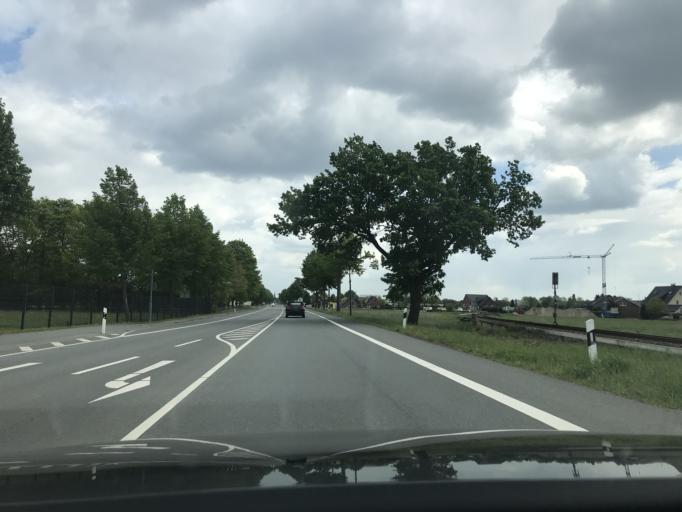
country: DE
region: North Rhine-Westphalia
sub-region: Regierungsbezirk Detmold
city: Rheda-Wiedenbruck
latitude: 51.8651
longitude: 8.2683
